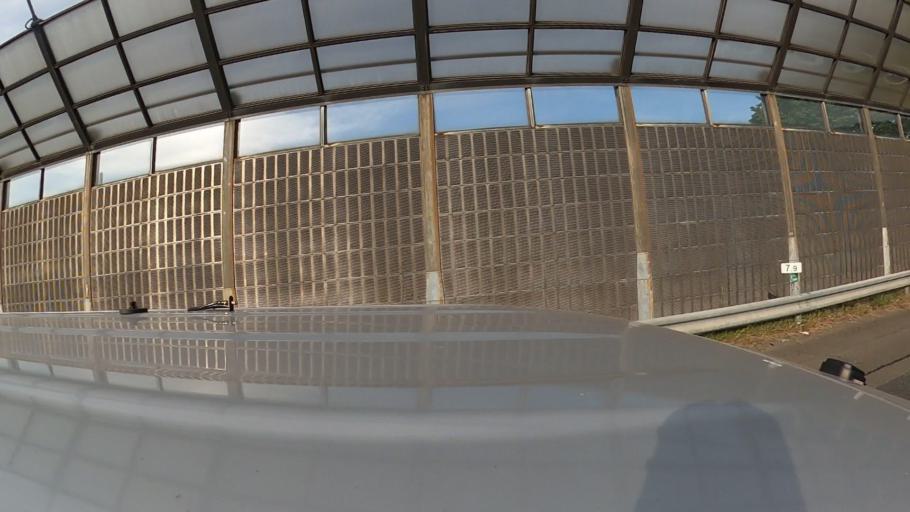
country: JP
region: Saitama
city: Shiki
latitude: 35.7984
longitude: 139.5410
